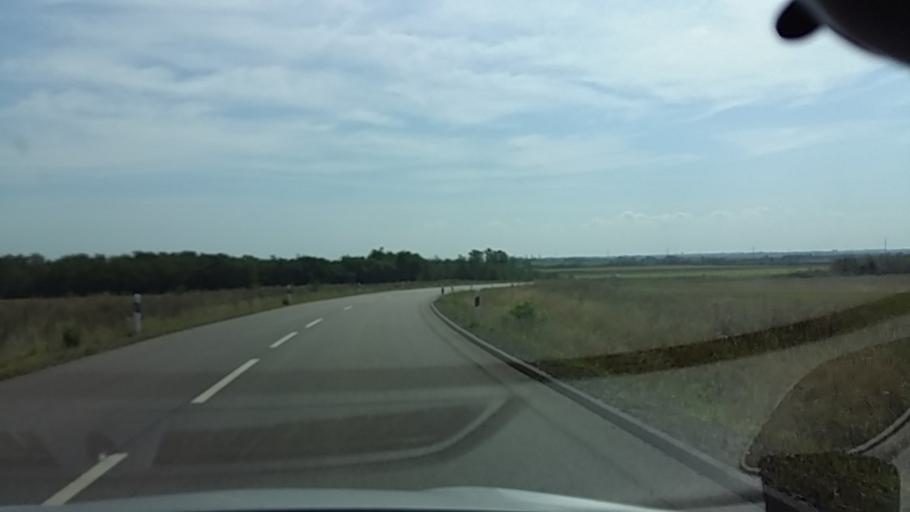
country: HU
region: Heves
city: Kompolt
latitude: 47.7722
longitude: 20.1784
